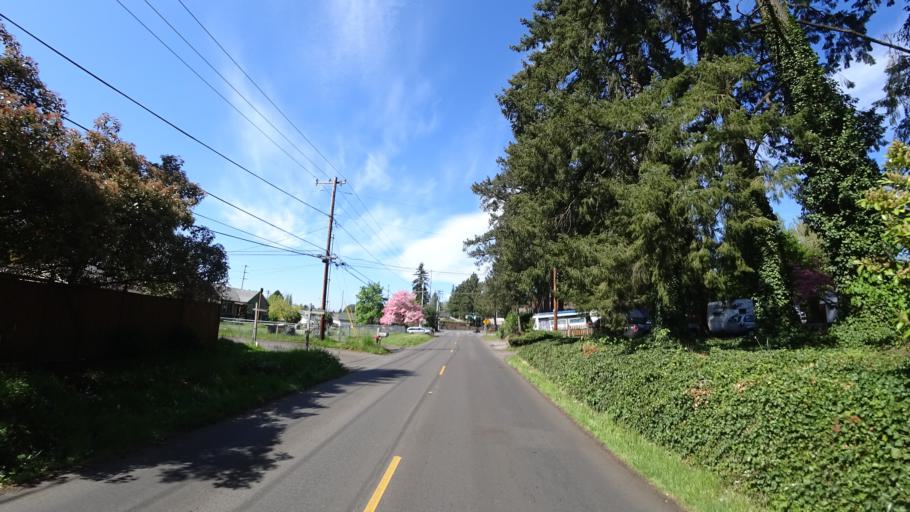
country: US
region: Oregon
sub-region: Washington County
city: Hillsboro
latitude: 45.5196
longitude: -122.9581
